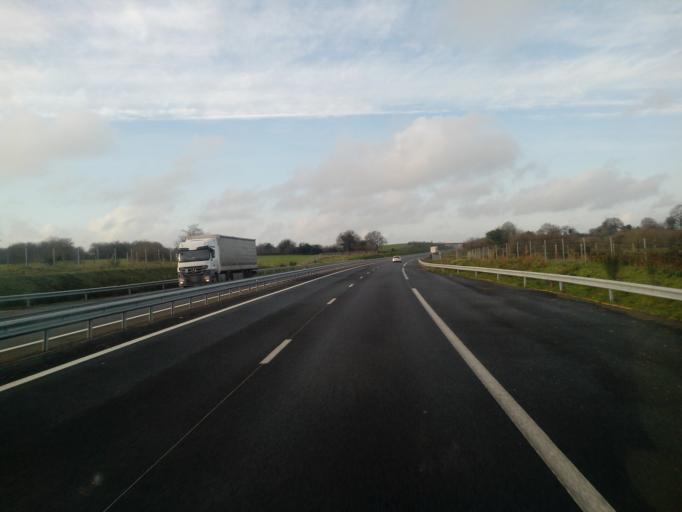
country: FR
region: Poitou-Charentes
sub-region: Departement des Deux-Sevres
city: Courlay
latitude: 46.8559
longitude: -0.5630
